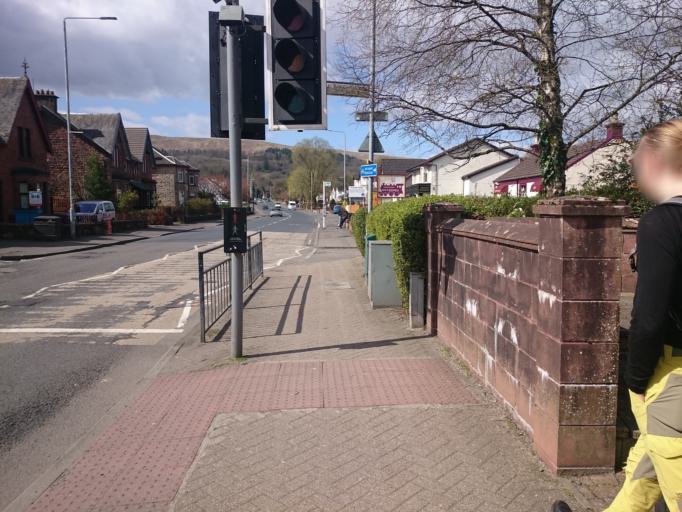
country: GB
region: Scotland
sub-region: West Dunbartonshire
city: Balloch
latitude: 56.0030
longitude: -4.5837
